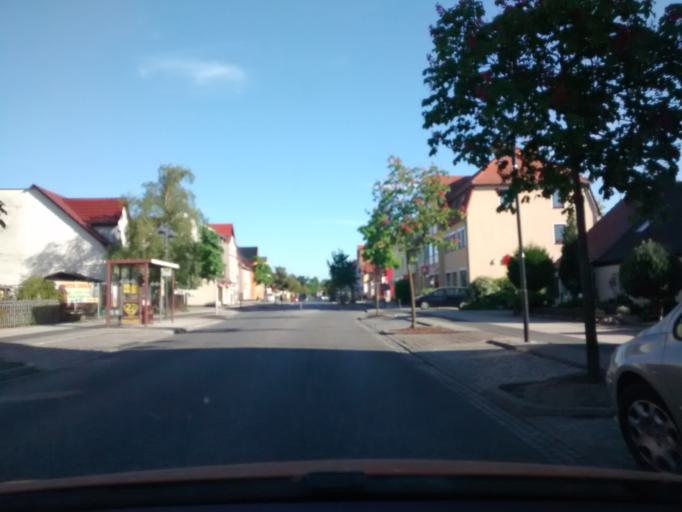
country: DE
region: Brandenburg
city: Furstenwalde
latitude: 52.3476
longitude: 14.0705
